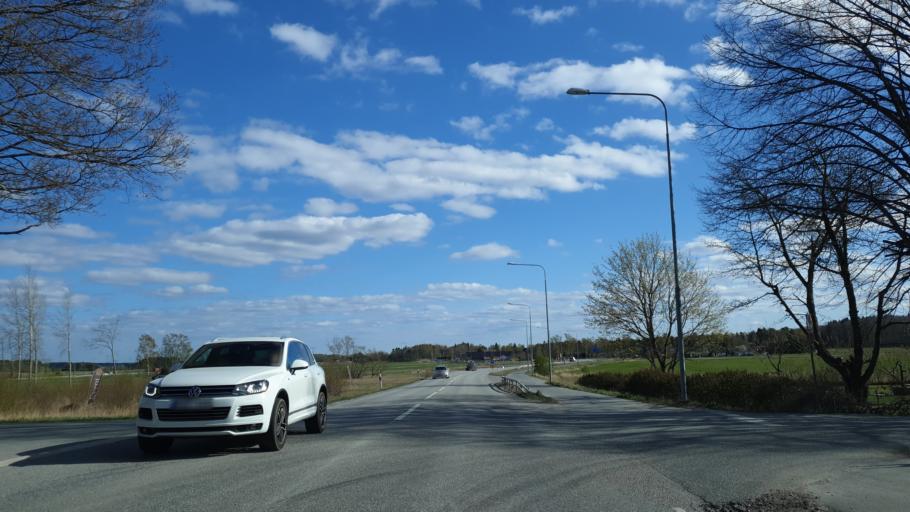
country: SE
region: Stockholm
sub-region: Sigtuna Kommun
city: Rosersberg
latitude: 59.5934
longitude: 17.8900
